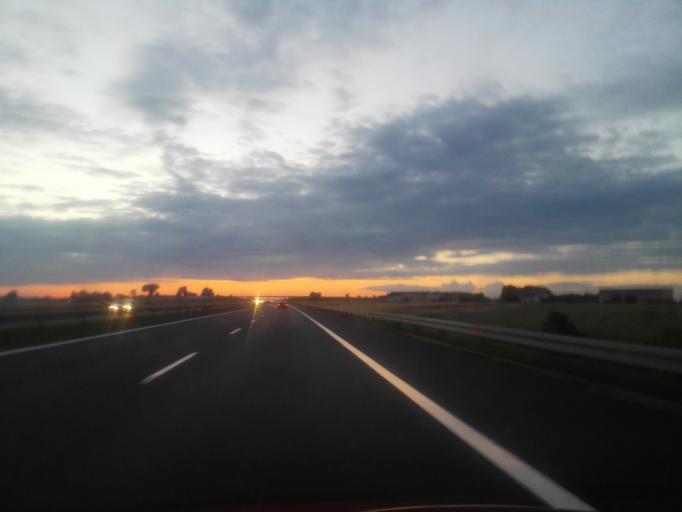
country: PL
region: Lodz Voivodeship
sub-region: Powiat piotrkowski
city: Moszczenica
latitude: 51.4719
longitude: 19.6308
